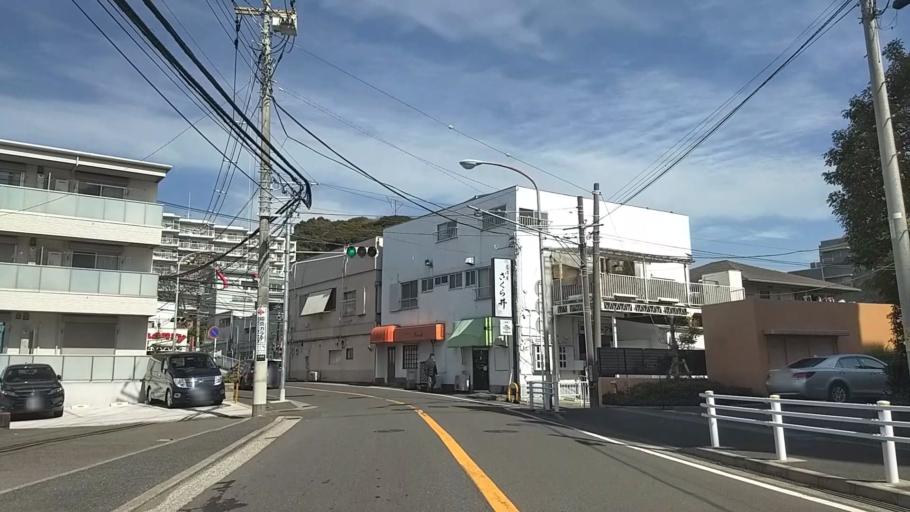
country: JP
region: Kanagawa
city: Fujisawa
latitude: 35.3925
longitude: 139.5278
